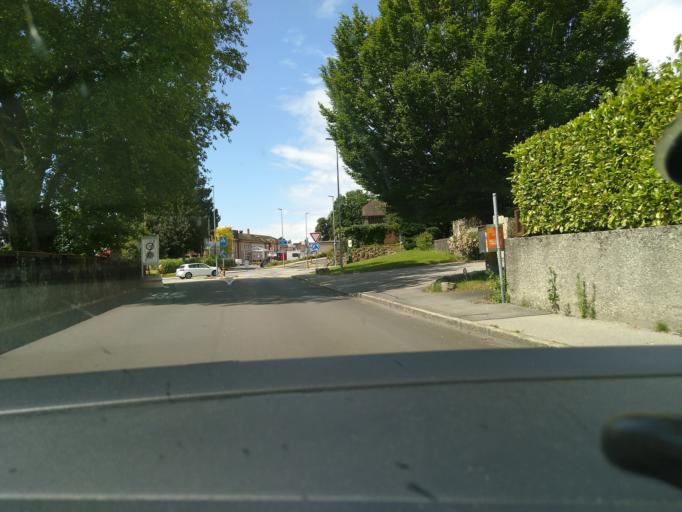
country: CH
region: Vaud
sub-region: Morges District
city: Aubonne
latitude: 46.4932
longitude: 6.3898
